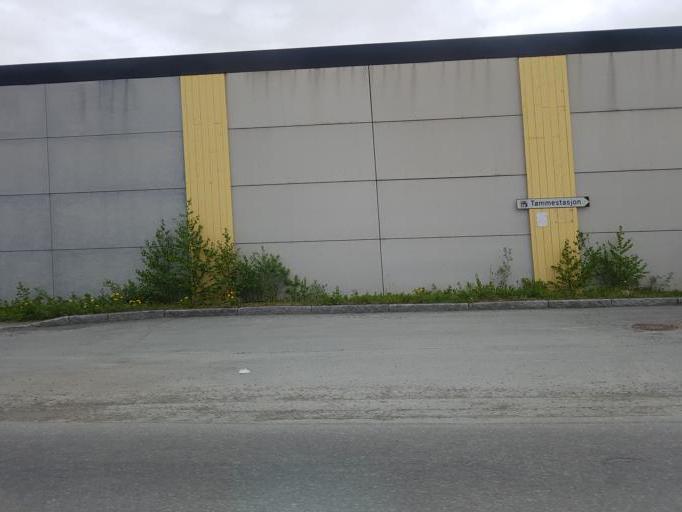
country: NO
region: Nord-Trondelag
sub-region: Levanger
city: Levanger
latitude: 63.7384
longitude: 11.2808
